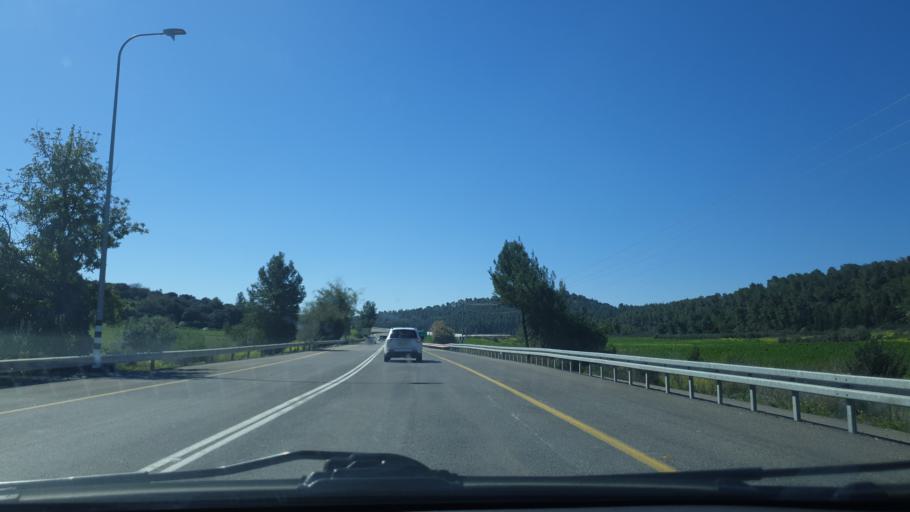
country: IL
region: Jerusalem
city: Bet Shemesh
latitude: 31.7012
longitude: 34.9429
